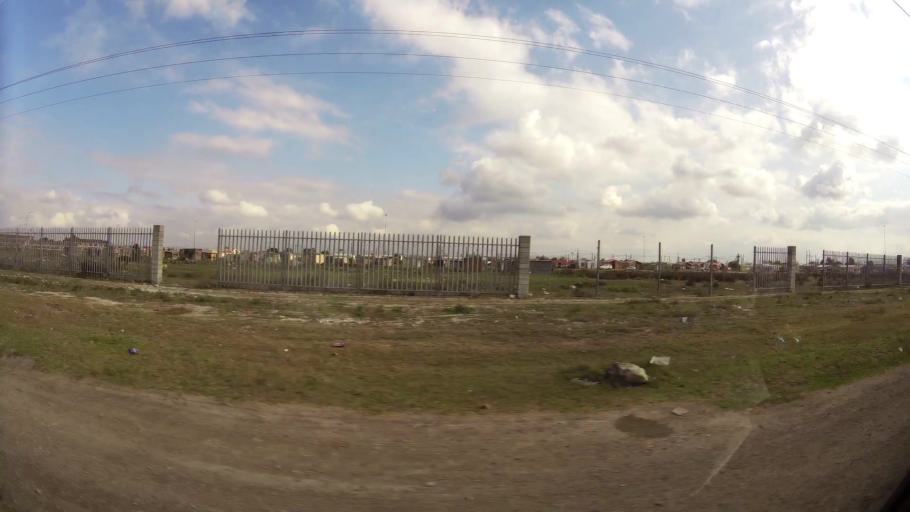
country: ZA
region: Eastern Cape
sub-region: Nelson Mandela Bay Metropolitan Municipality
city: Port Elizabeth
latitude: -33.7843
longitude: 25.5923
